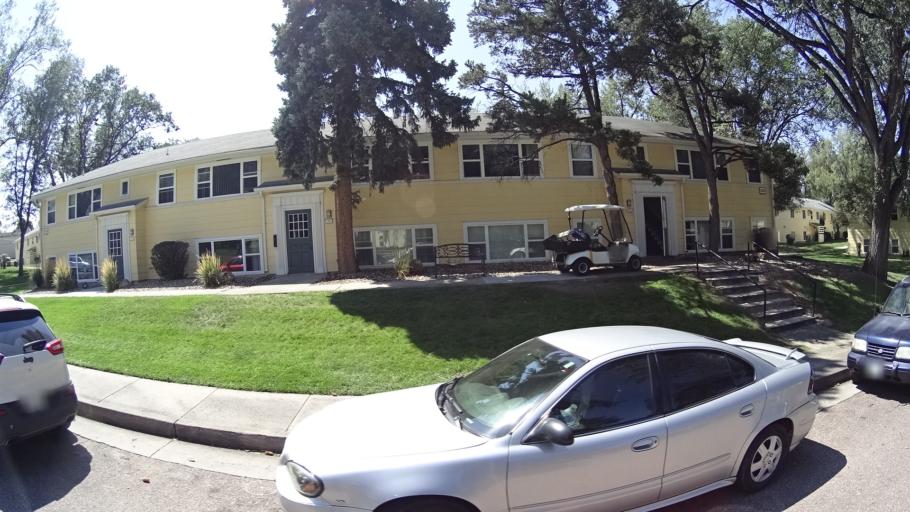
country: US
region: Colorado
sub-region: El Paso County
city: Colorado Springs
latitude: 38.8512
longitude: -104.8013
